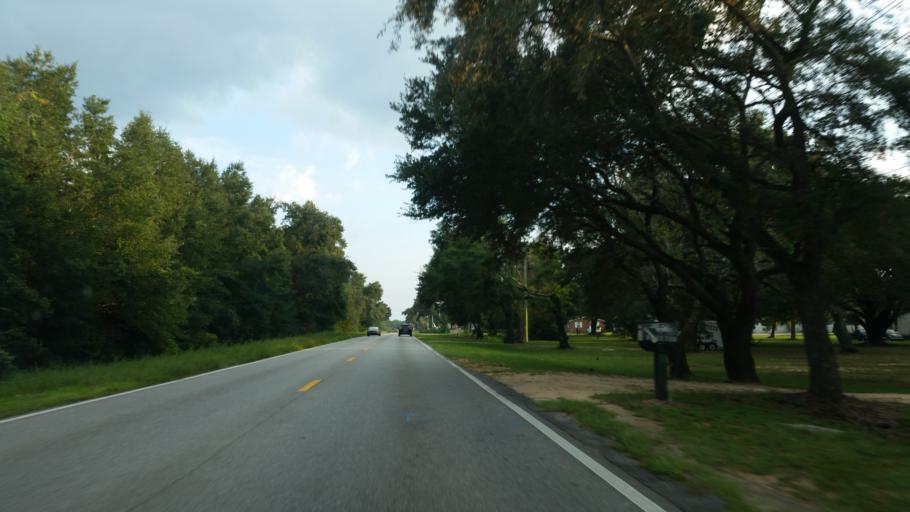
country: US
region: Florida
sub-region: Santa Rosa County
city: Pace
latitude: 30.5853
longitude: -87.1117
